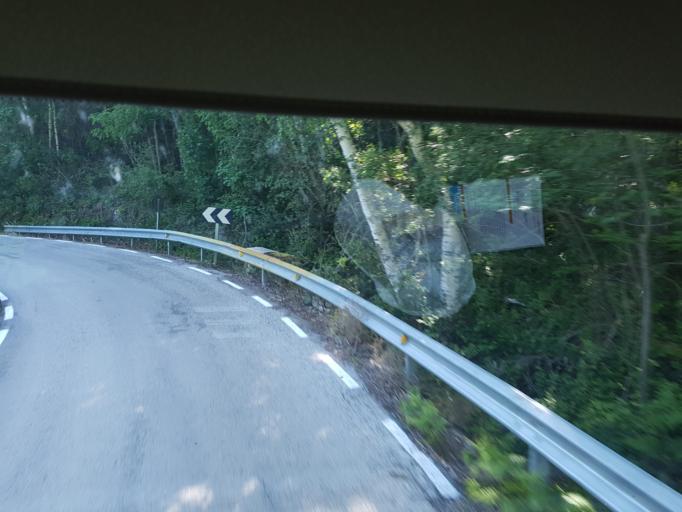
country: ES
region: Castille and Leon
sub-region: Provincia de Burgos
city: Espinosa de los Monteros
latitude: 43.1234
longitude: -3.5807
